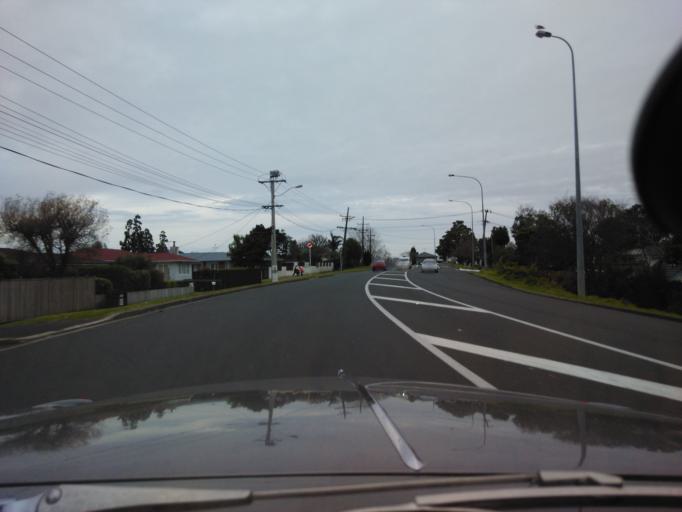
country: NZ
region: Auckland
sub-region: Auckland
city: North Shore
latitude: -36.7693
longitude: 174.7265
